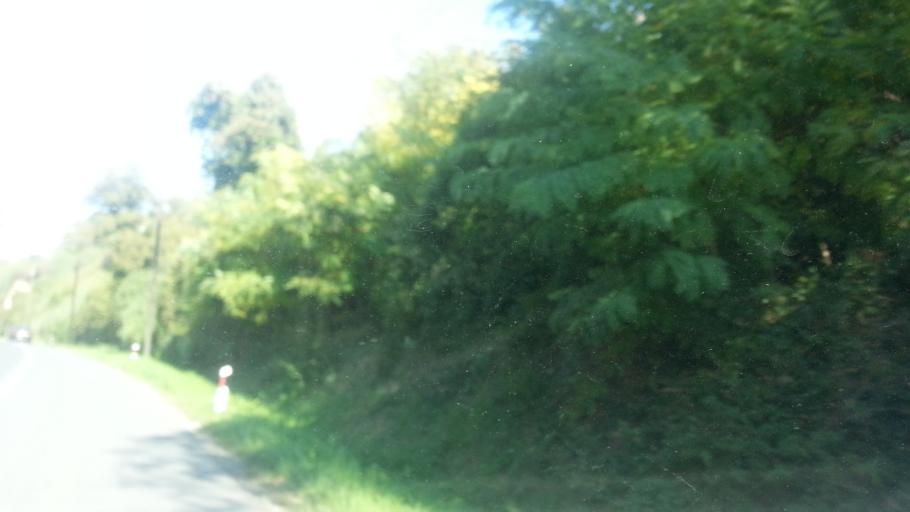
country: RS
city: Novi Slankamen
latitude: 45.1367
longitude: 20.2537
